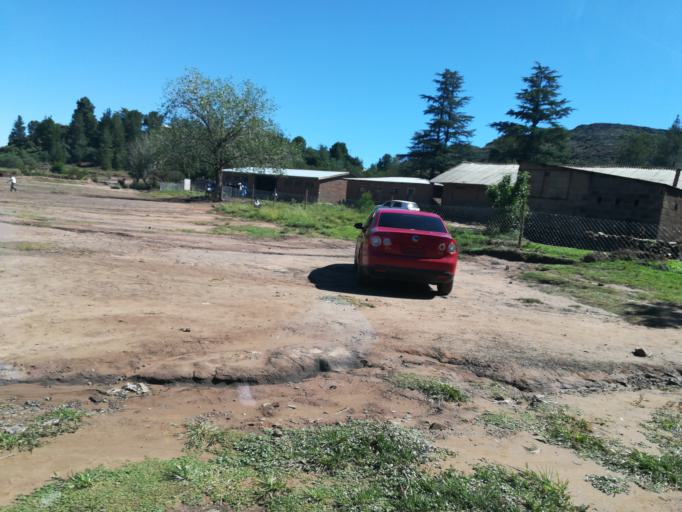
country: LS
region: Quthing
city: Quthing
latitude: -30.3431
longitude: 27.5436
